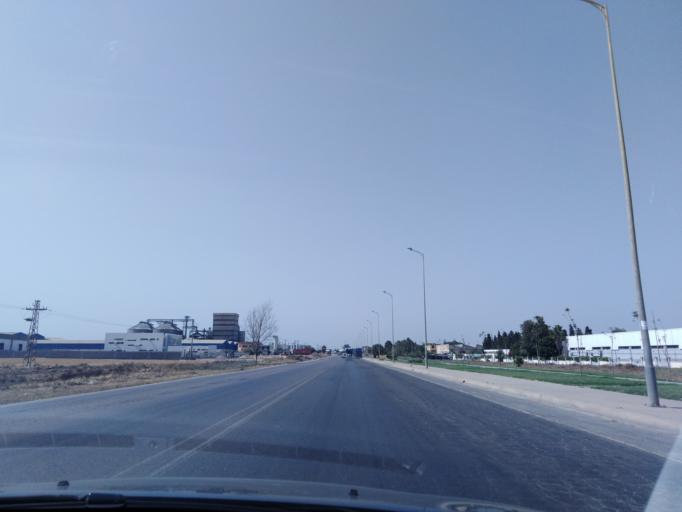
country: MA
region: Chaouia-Ouardigha
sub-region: Settat Province
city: Berrechid
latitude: 33.2431
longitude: -7.5869
